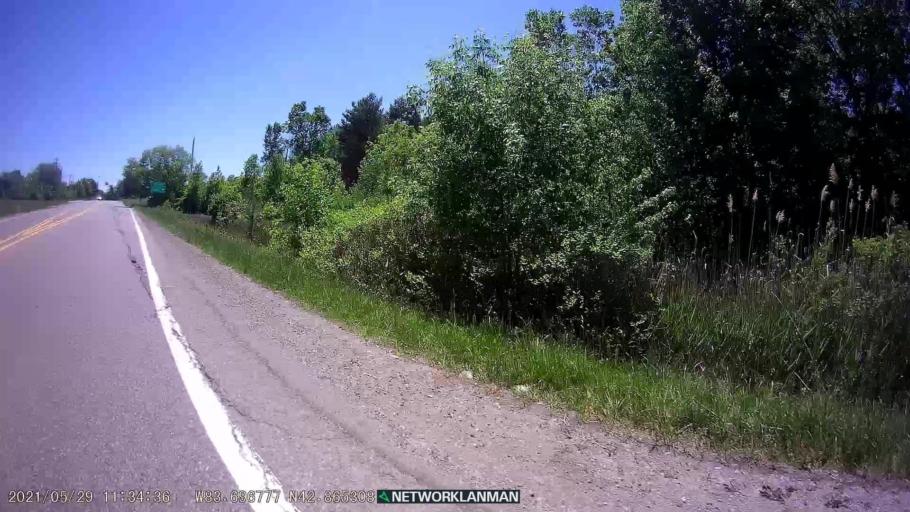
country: US
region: Michigan
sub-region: Genesee County
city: Lake Fenton
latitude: 42.8652
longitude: -83.6968
